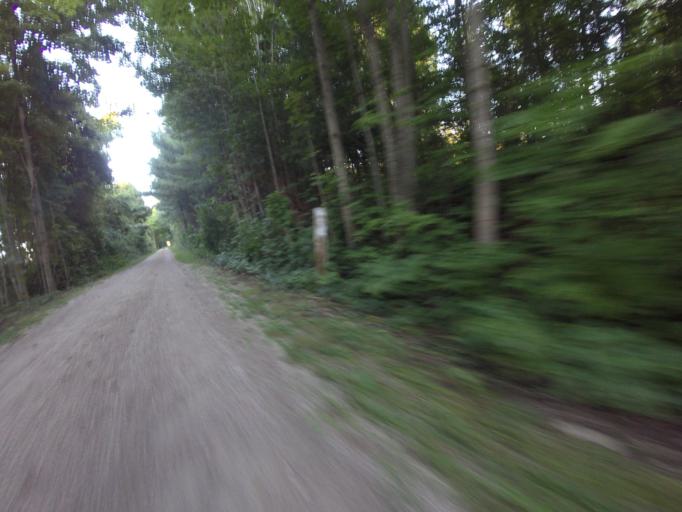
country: CA
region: Ontario
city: Goderich
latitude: 43.7592
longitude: -81.6897
